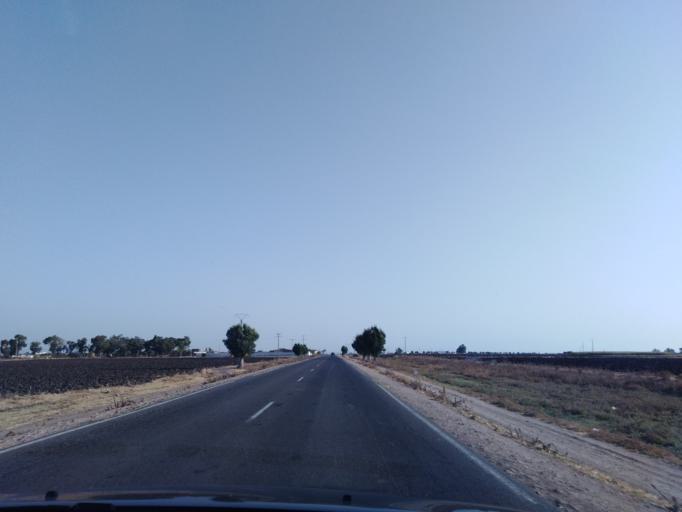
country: MA
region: Doukkala-Abda
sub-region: Safi
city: Youssoufia
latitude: 32.4749
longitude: -8.7715
